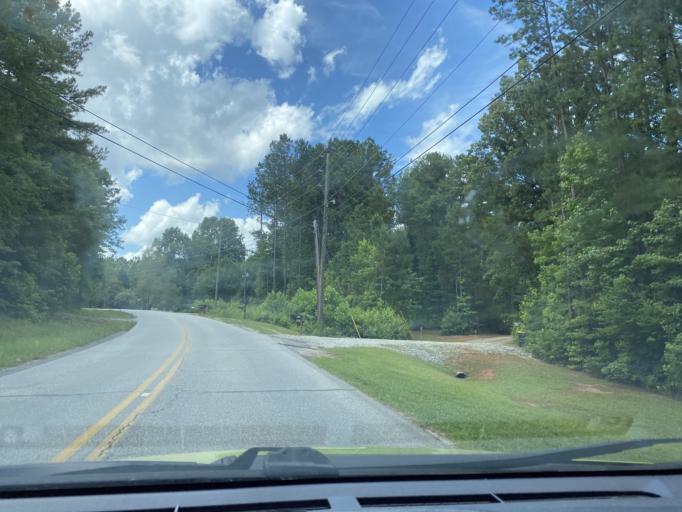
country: US
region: Georgia
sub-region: Fayette County
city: Peachtree City
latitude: 33.4118
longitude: -84.6922
